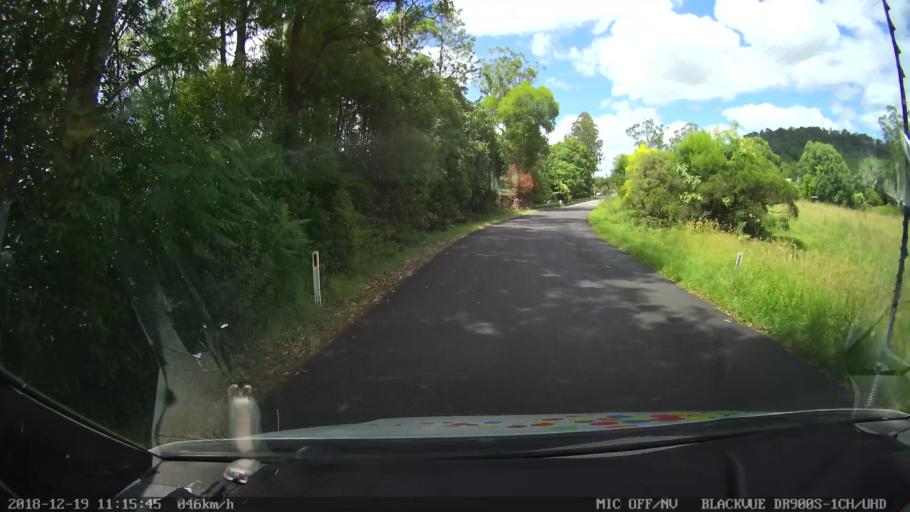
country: AU
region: New South Wales
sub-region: Lismore Municipality
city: Nimbin
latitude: -28.6703
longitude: 153.2787
